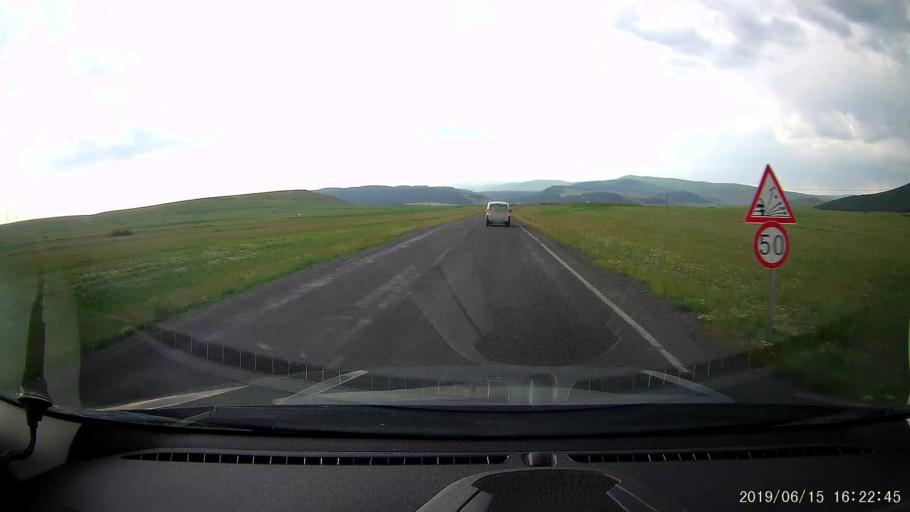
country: TR
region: Ardahan
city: Hanak
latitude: 41.1851
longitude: 42.8541
